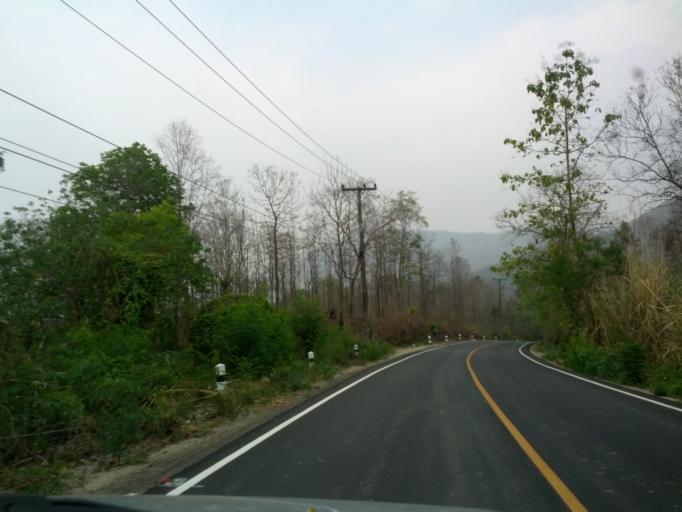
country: TH
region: Chiang Mai
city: Mae Taeng
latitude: 19.1021
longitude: 99.0777
